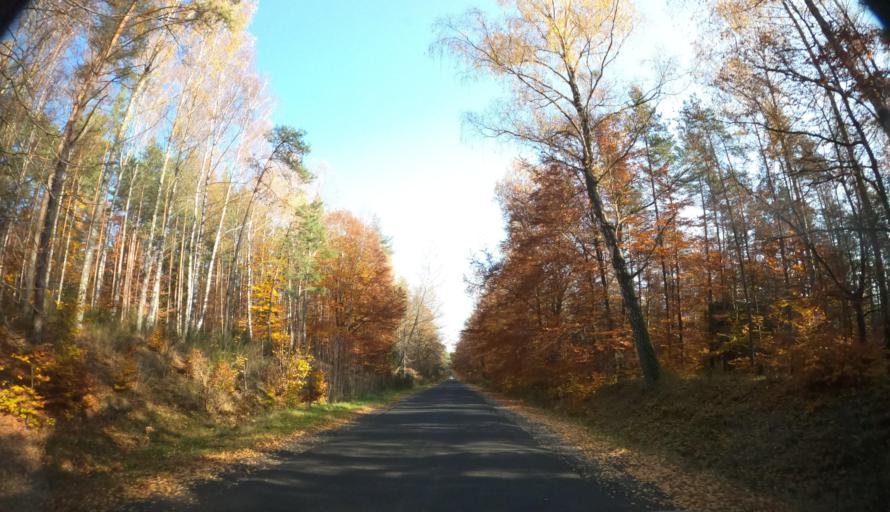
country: PL
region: West Pomeranian Voivodeship
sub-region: Powiat koszalinski
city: Polanow
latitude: 54.2353
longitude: 16.7459
